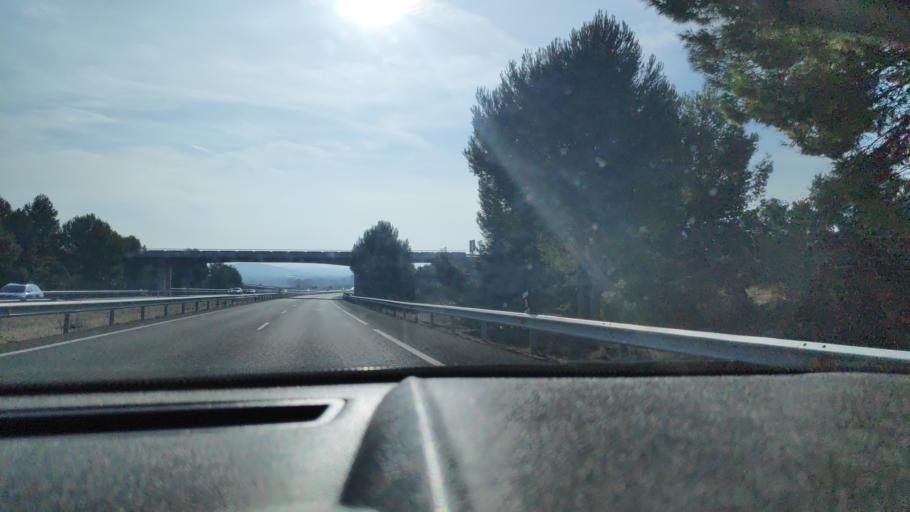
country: ES
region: Andalusia
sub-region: Provincia de Jaen
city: Mengibar
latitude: 37.9101
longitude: -3.7857
